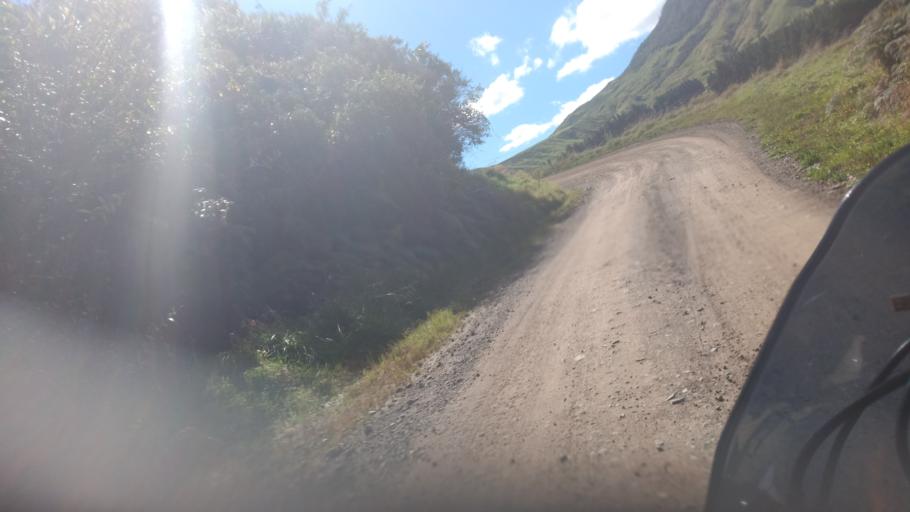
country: NZ
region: Bay of Plenty
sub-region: Opotiki District
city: Opotiki
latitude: -38.3432
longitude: 177.5826
